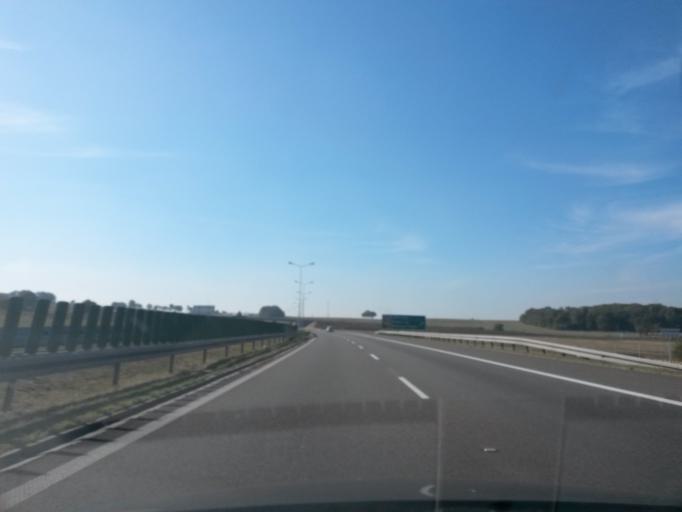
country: PL
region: Opole Voivodeship
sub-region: Powiat strzelecki
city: Strzelce Opolskie
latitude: 50.4589
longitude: 18.2787
